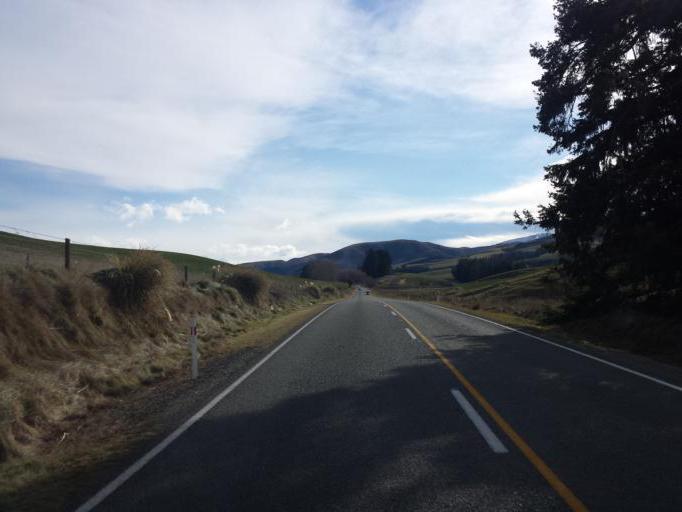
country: NZ
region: Canterbury
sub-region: Timaru District
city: Pleasant Point
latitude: -44.1021
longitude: 171.0031
